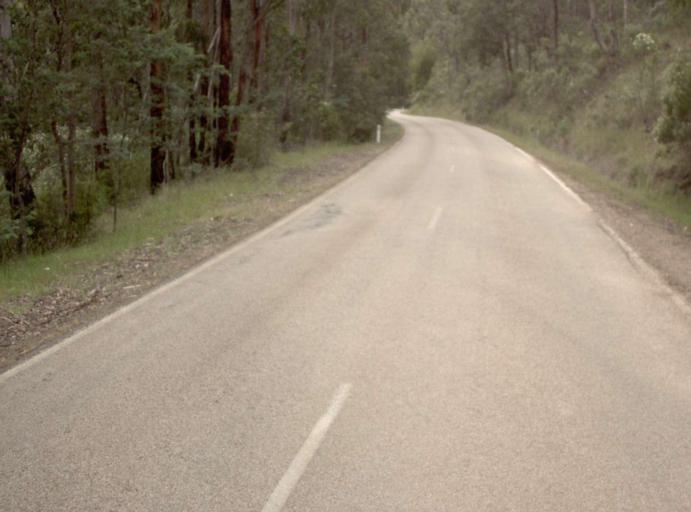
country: AU
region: Victoria
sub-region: East Gippsland
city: Bairnsdale
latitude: -37.6173
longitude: 147.1915
